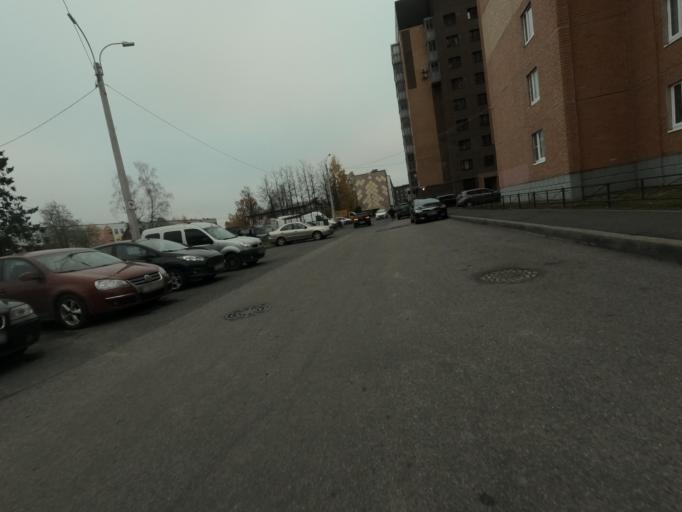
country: RU
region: Leningrad
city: Kirovsk
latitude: 59.8852
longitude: 30.9933
